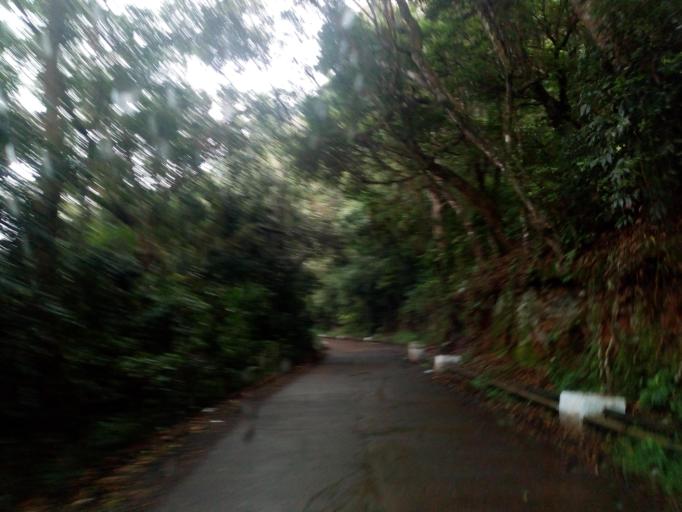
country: IN
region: Tamil Nadu
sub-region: Nilgiri
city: Wellington
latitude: 11.3502
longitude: 76.8294
